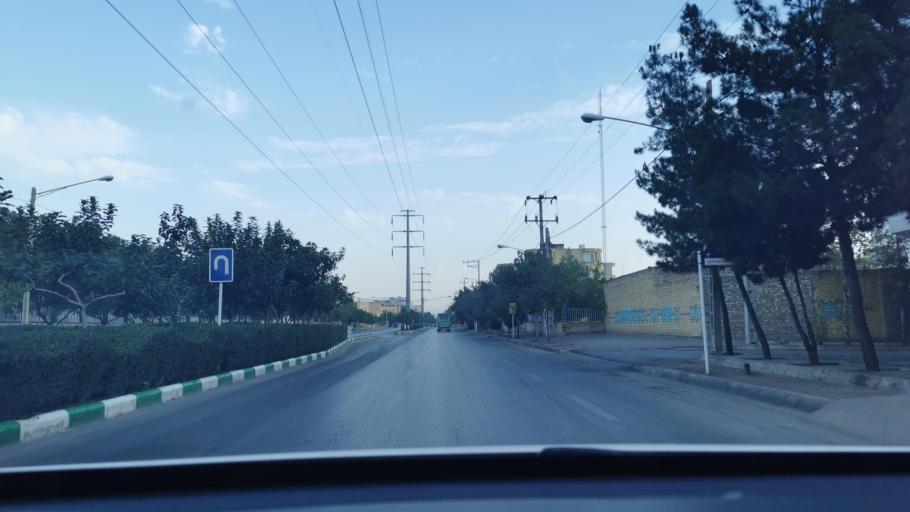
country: IR
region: Razavi Khorasan
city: Mashhad
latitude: 36.3527
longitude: 59.5290
